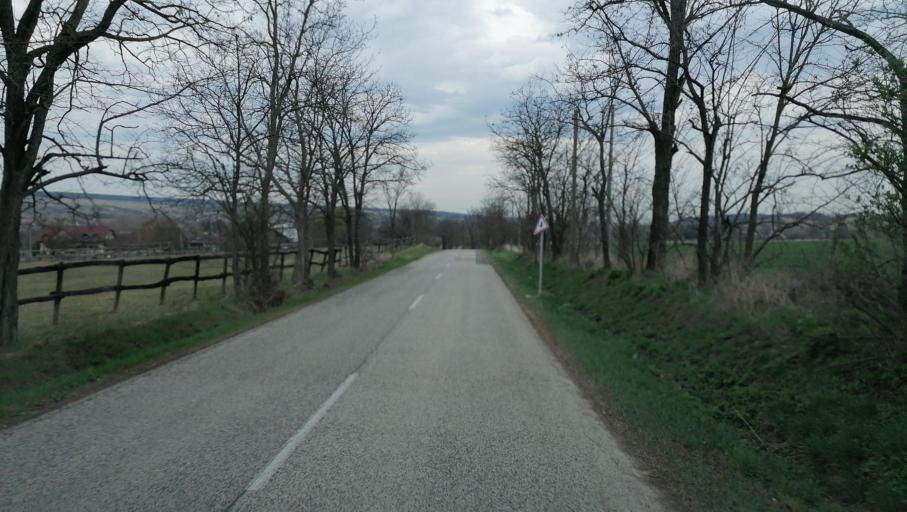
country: HU
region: Pest
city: Soskut
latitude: 47.4074
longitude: 18.8112
